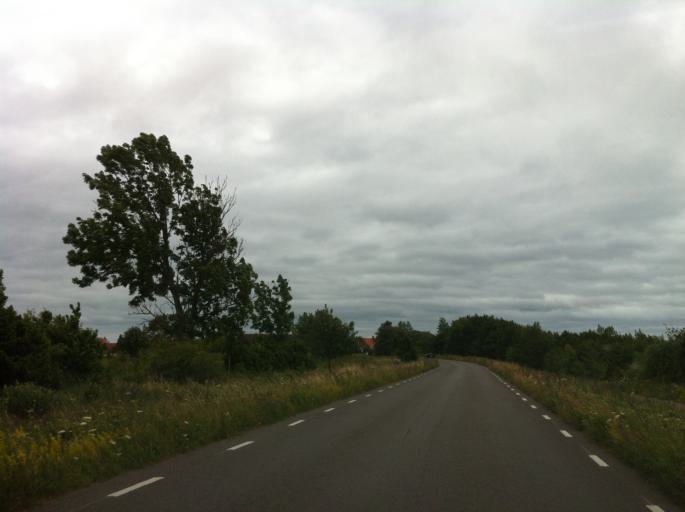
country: SE
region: Kalmar
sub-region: Oskarshamns Kommun
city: Oskarshamn
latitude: 57.3190
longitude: 16.9967
